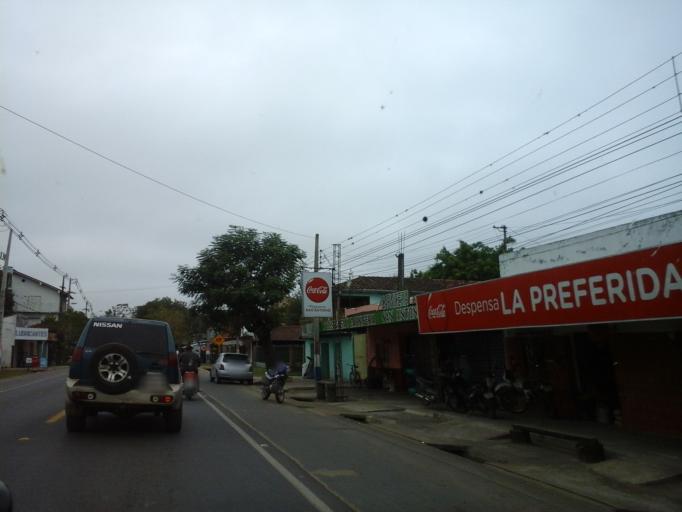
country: PY
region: Neembucu
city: Pilar
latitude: -26.8491
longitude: -58.2941
